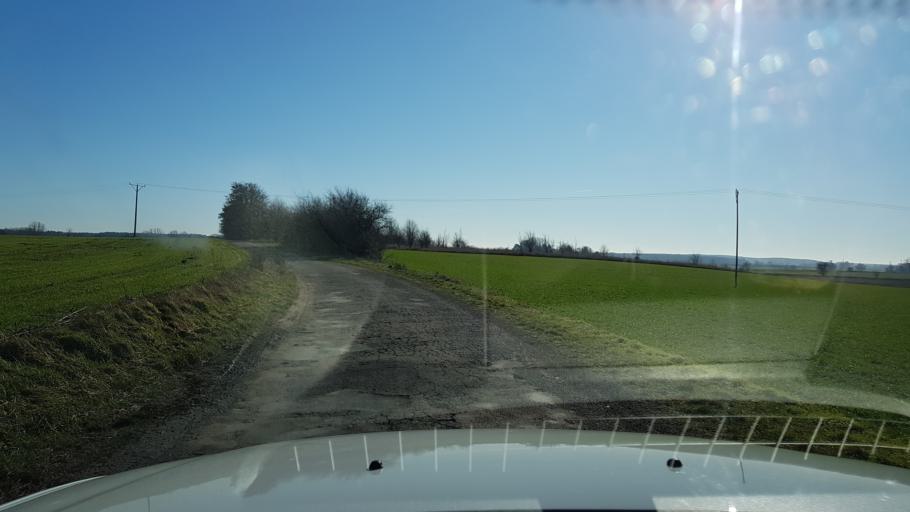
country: PL
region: West Pomeranian Voivodeship
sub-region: Powiat pyrzycki
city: Przelewice
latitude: 53.0303
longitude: 15.0694
